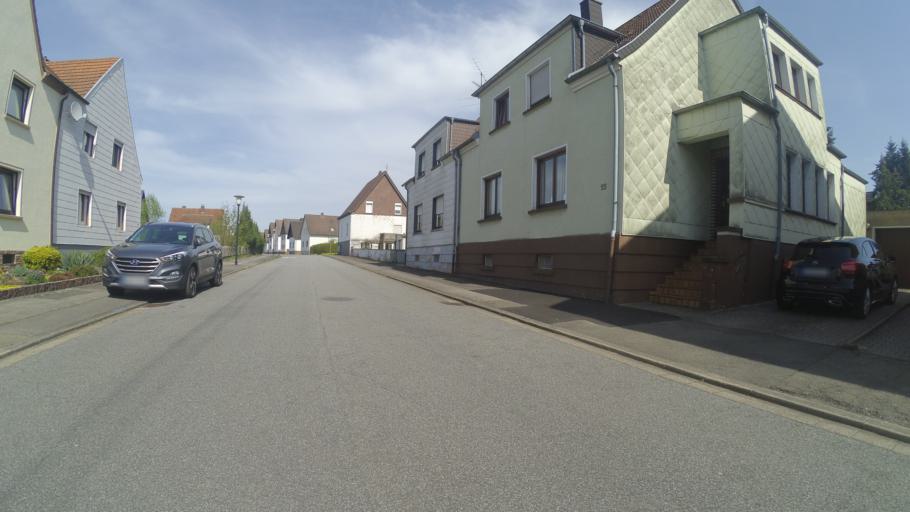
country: DE
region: Saarland
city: Homburg
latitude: 49.3090
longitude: 7.3110
